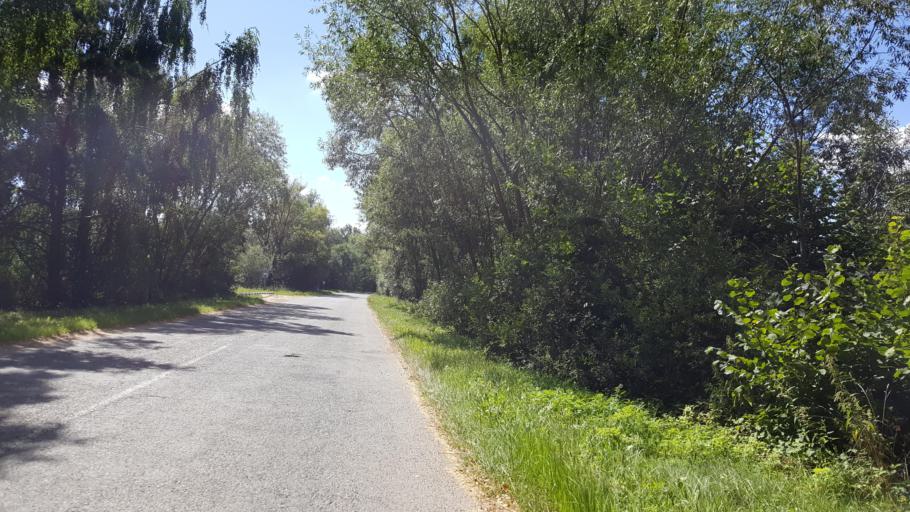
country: BY
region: Brest
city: Horad Kobryn
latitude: 52.2991
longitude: 24.3524
